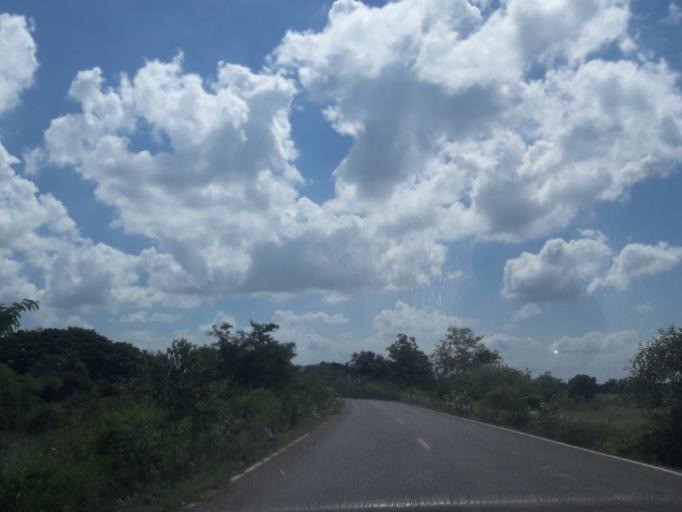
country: TH
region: Lop Buri
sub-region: Amphoe Tha Luang
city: Tha Luang
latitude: 15.0610
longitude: 101.0322
